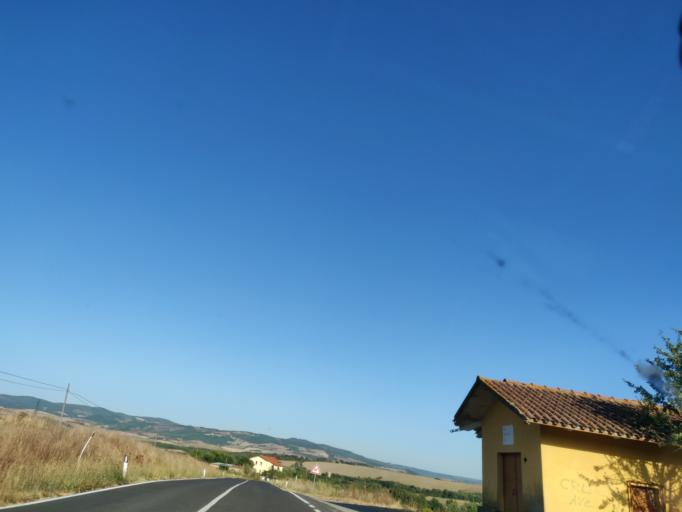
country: IT
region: Tuscany
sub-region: Provincia di Siena
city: Piancastagnaio
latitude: 42.8166
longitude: 11.7423
